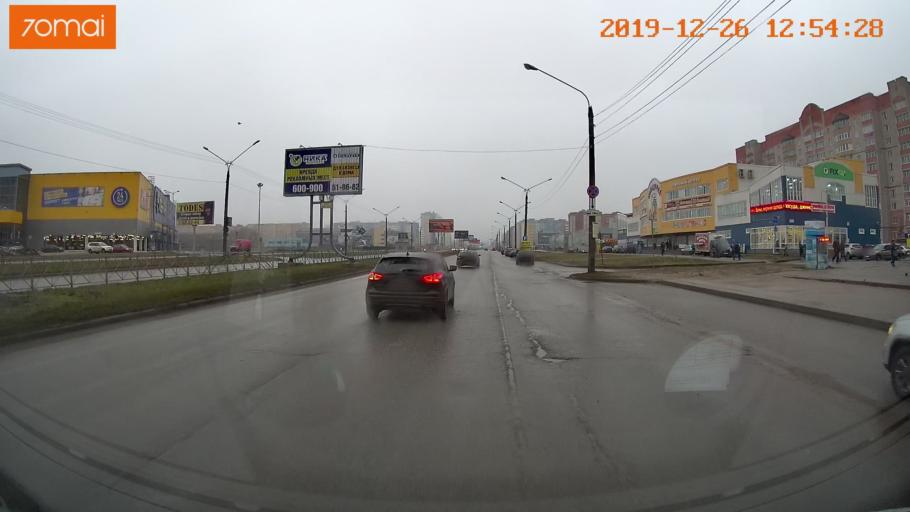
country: RU
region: Vologda
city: Cherepovets
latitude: 59.0928
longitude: 37.9146
